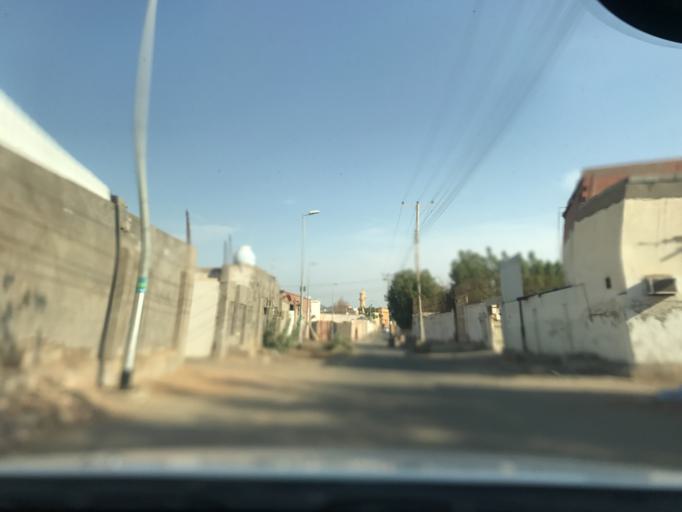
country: SA
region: Makkah
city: Al Jumum
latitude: 21.4468
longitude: 39.5333
